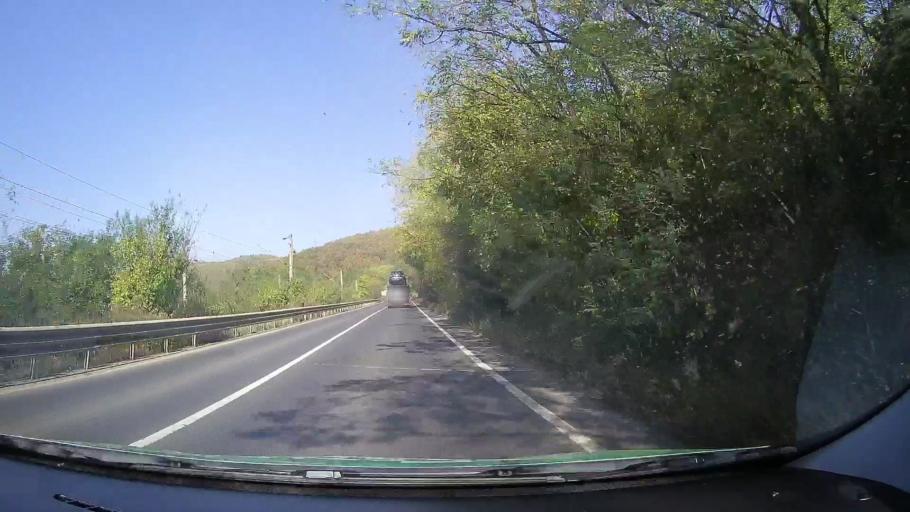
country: RO
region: Arad
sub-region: Comuna Bata
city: Bata
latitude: 46.0449
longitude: 22.0593
